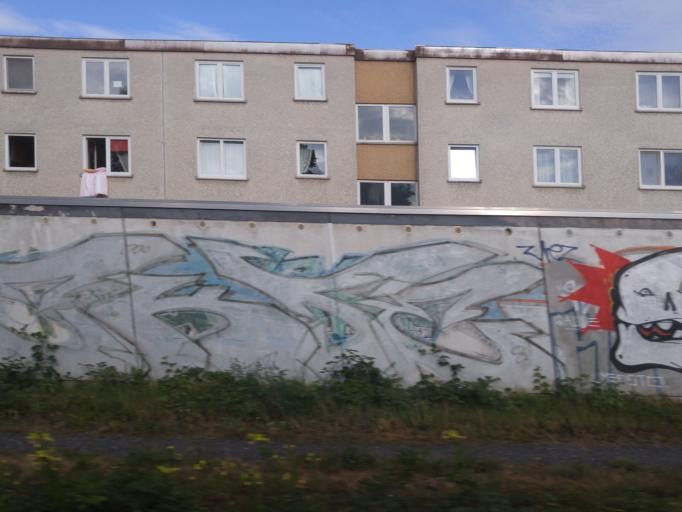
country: DE
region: Hesse
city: Langen
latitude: 49.9856
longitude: 8.6556
